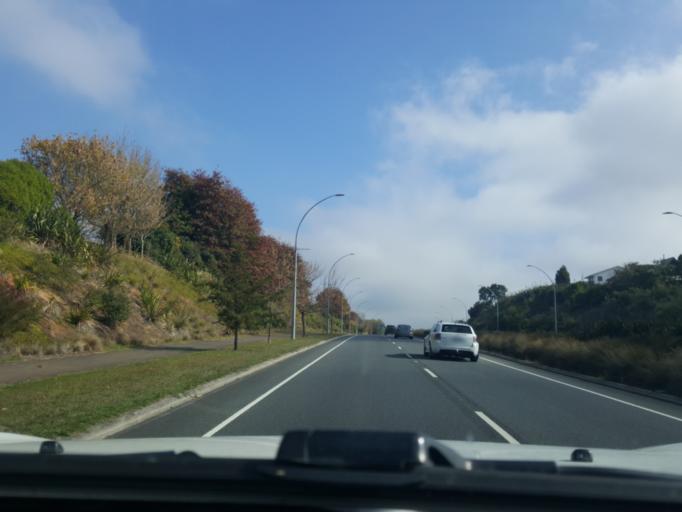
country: NZ
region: Waikato
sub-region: Hamilton City
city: Hamilton
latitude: -37.7463
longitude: 175.2459
